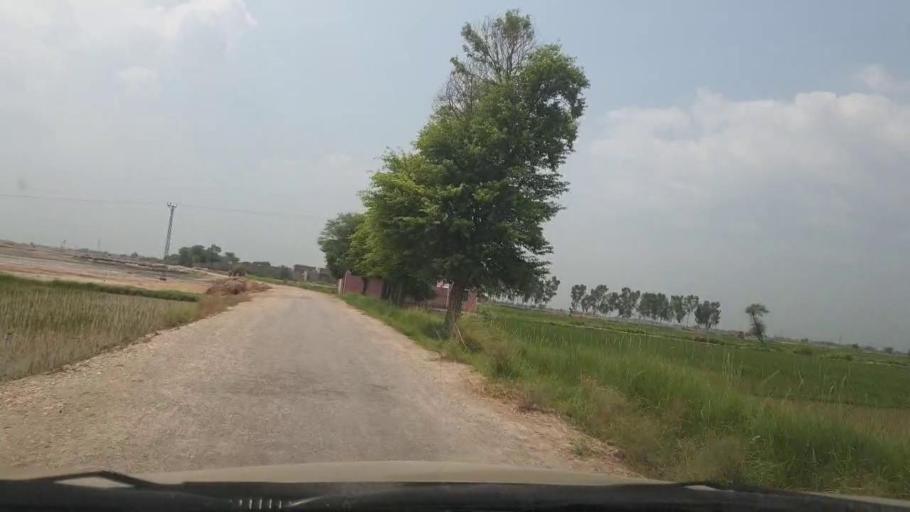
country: PK
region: Sindh
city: Naudero
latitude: 27.6946
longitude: 68.2576
